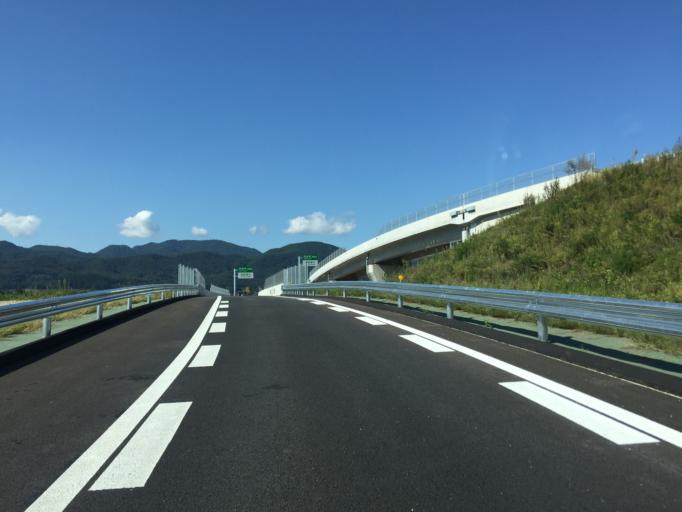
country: JP
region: Fukushima
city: Fukushima-shi
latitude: 37.7890
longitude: 140.4168
